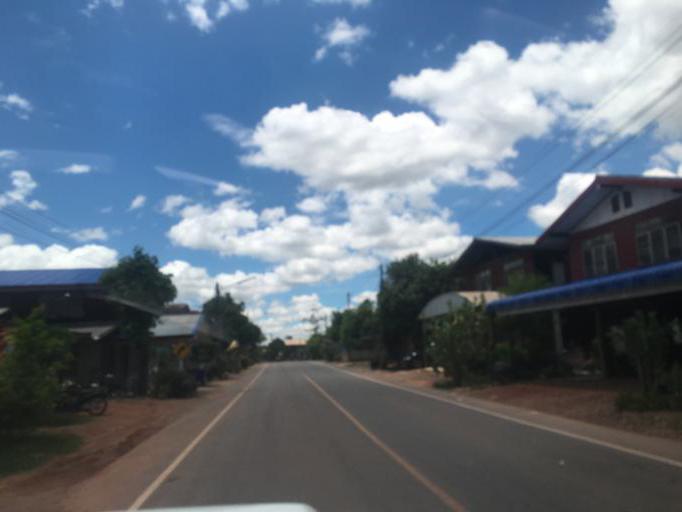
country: TH
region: Changwat Udon Thani
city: Nong Saeng
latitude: 17.1766
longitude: 102.7718
